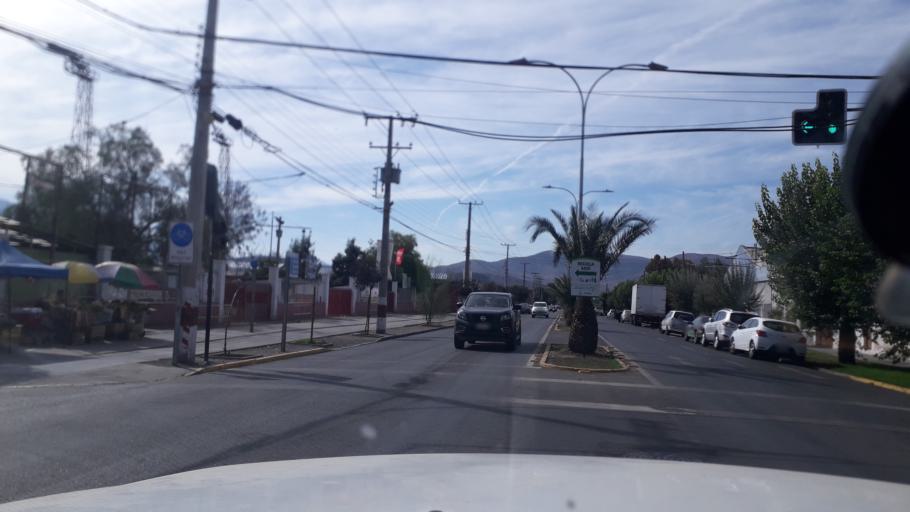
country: CL
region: Valparaiso
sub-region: Provincia de San Felipe
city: San Felipe
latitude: -32.7480
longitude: -70.7292
